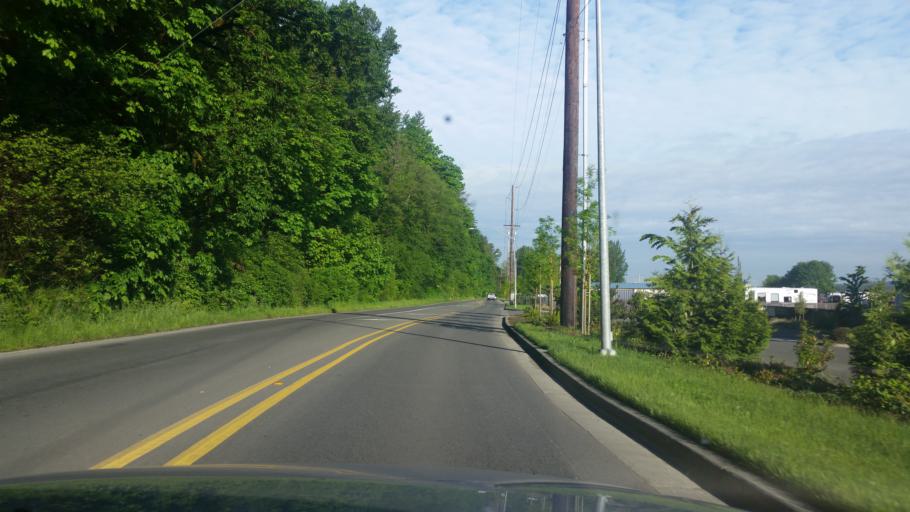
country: US
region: Washington
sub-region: Pierce County
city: Alderton
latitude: 47.1819
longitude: -122.2461
